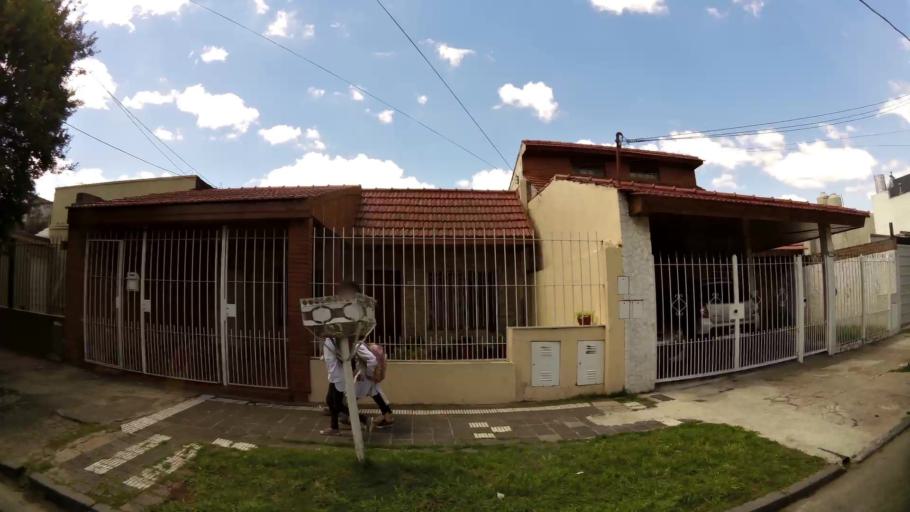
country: AR
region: Buenos Aires
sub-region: Partido de Lanus
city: Lanus
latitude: -34.7293
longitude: -58.4079
